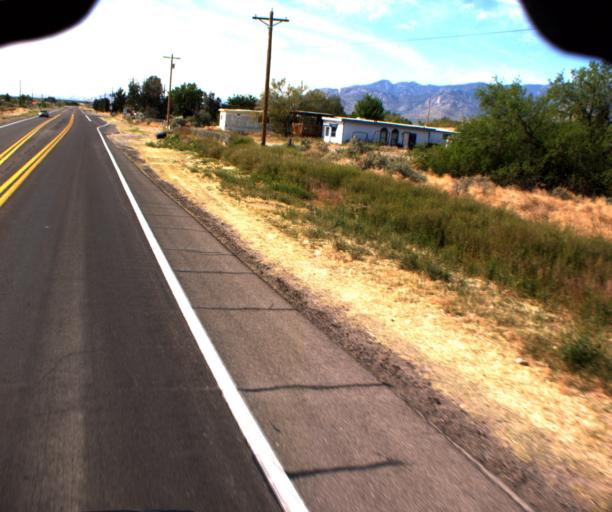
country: US
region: Arizona
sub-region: Graham County
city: Cactus Flat
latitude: 32.7448
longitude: -109.7164
